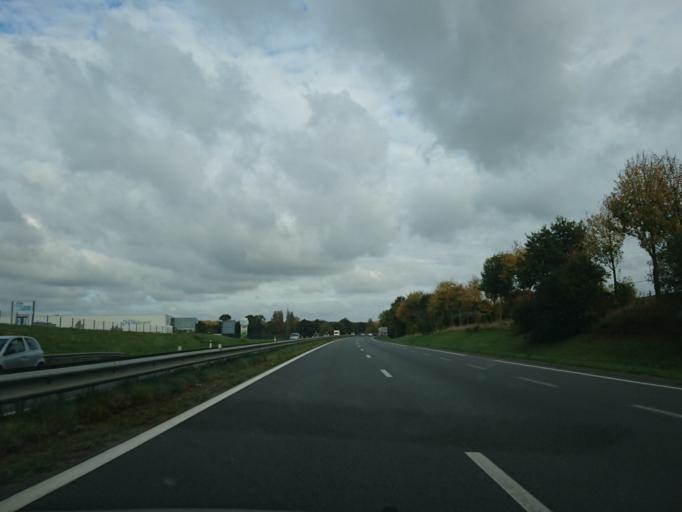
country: FR
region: Brittany
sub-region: Departement des Cotes-d'Armor
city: Pommeret
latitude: 48.4812
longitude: -2.6419
